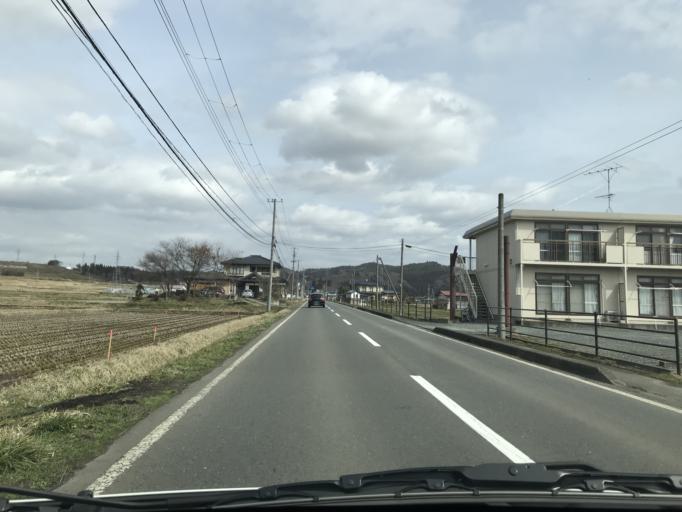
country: JP
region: Iwate
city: Mizusawa
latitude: 39.2005
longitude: 141.1874
